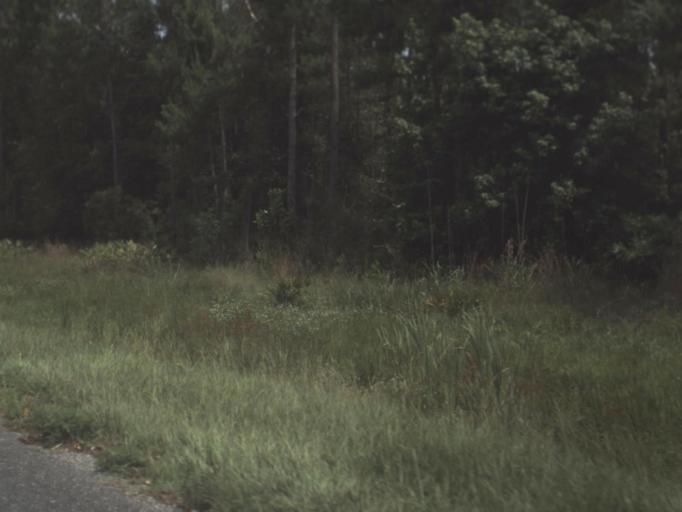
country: US
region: Florida
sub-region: Taylor County
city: Perry
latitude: 29.9741
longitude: -83.4830
